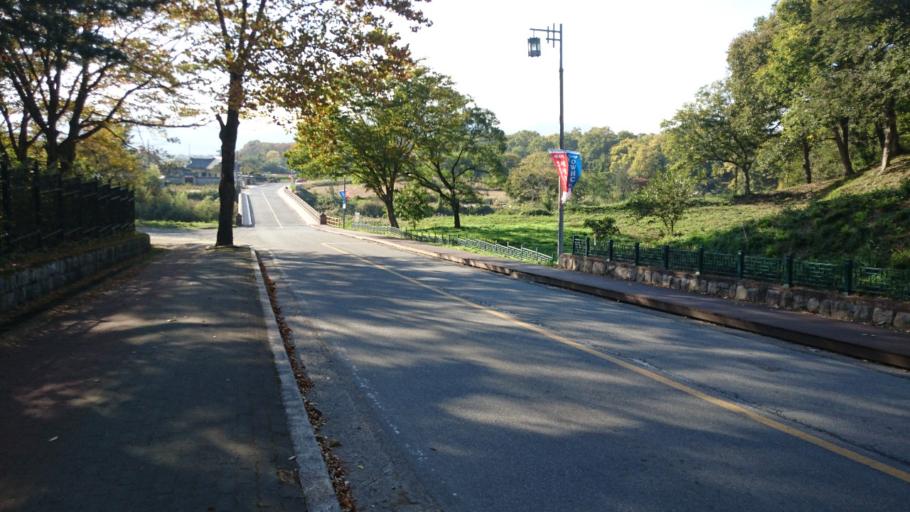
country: KR
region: Gyeongsangbuk-do
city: Kyonju
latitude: 35.8302
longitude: 129.2272
